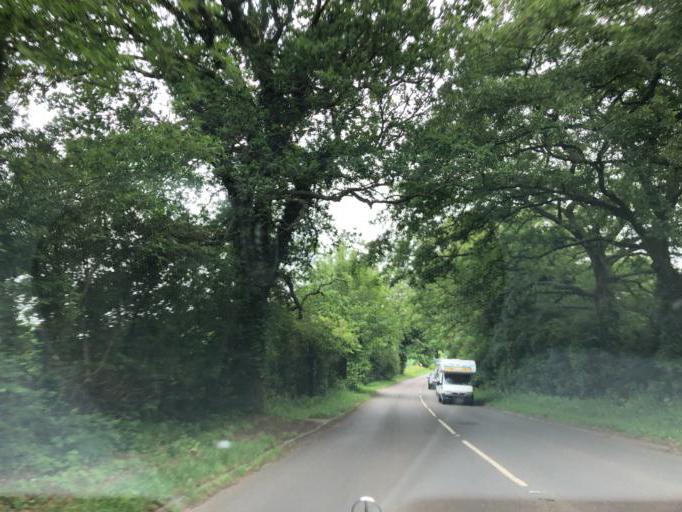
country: GB
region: England
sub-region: Solihull
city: Balsall Common
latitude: 52.3711
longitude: -1.6367
